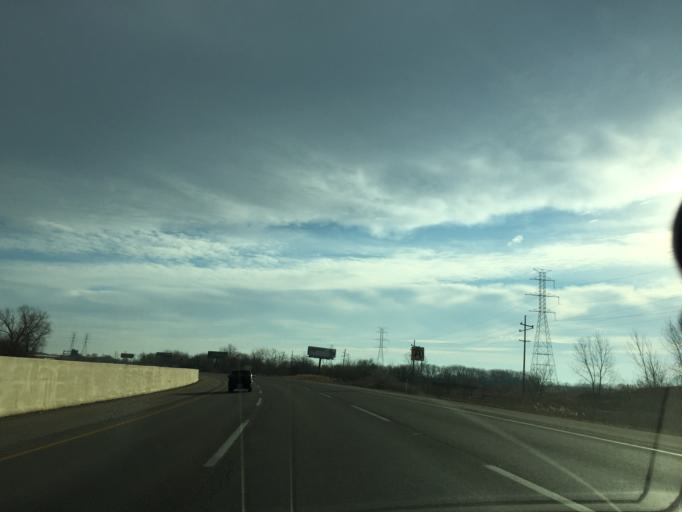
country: US
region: Indiana
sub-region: Lake County
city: New Chicago
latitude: 41.5850
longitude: -87.2970
